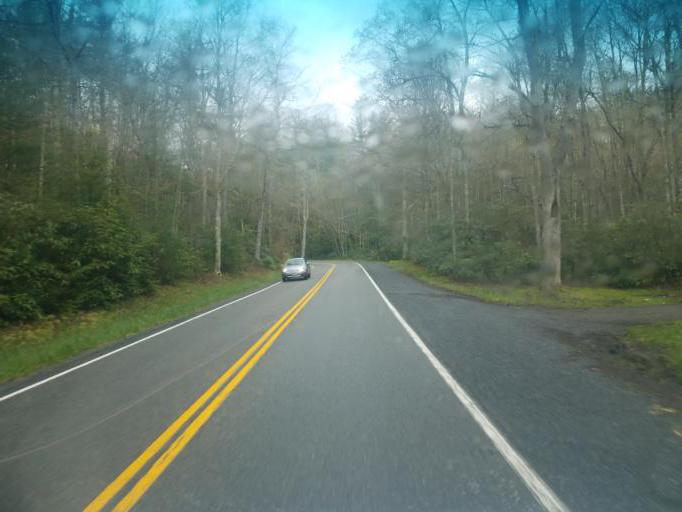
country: US
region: Virginia
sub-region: Smyth County
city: Chilhowie
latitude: 36.6474
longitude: -81.7073
